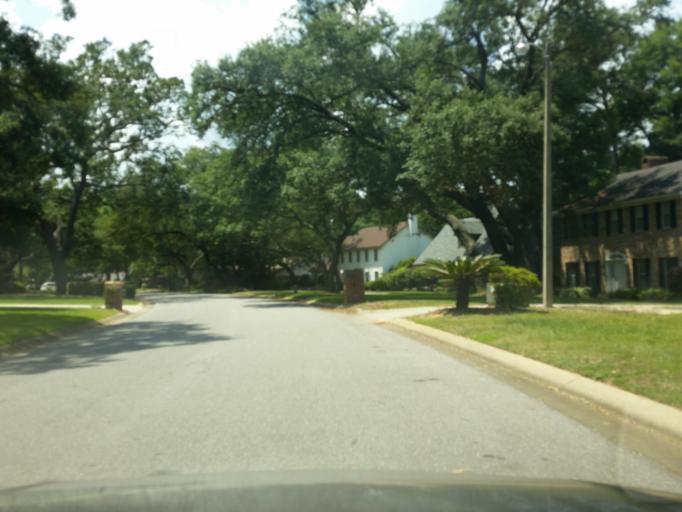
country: US
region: Florida
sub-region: Escambia County
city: Ferry Pass
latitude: 30.5026
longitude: -87.1625
